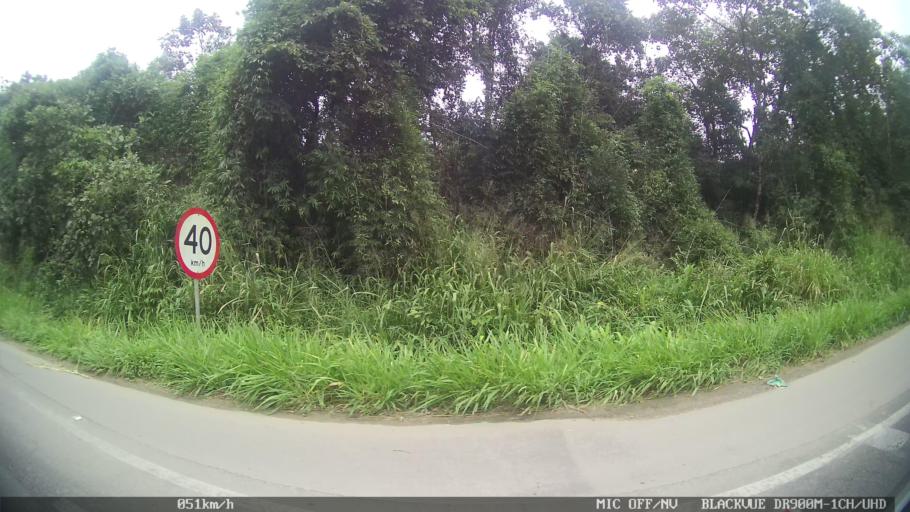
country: BR
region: Santa Catarina
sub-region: Joinville
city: Joinville
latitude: -26.3043
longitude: -48.9200
